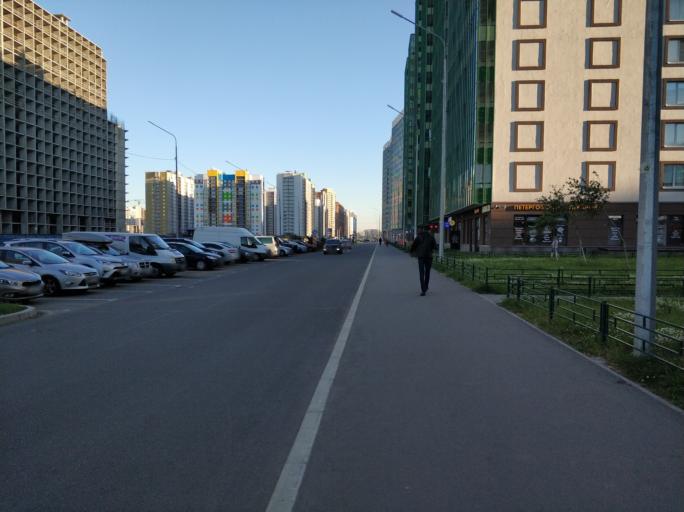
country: RU
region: Leningrad
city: Murino
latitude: 60.0642
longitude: 30.4337
